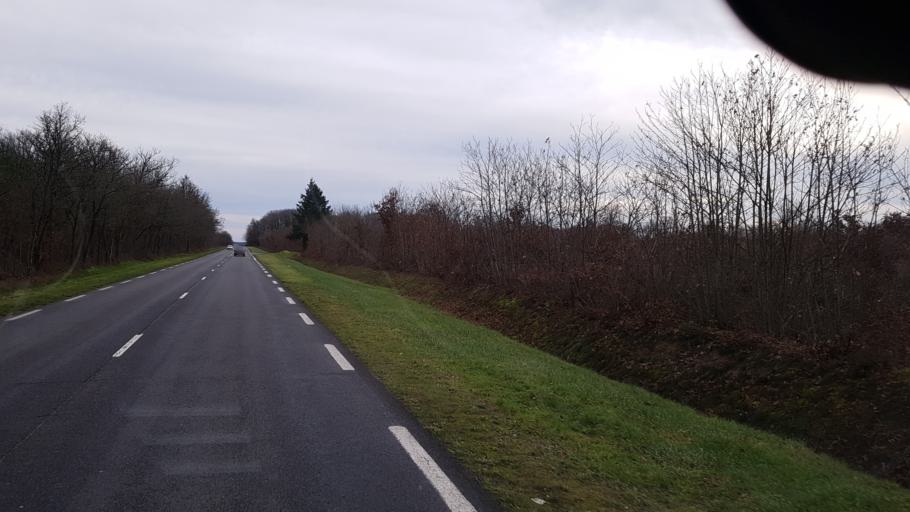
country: FR
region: Centre
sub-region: Departement du Loir-et-Cher
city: Lamotte-Beuvron
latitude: 47.6225
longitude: 2.0115
